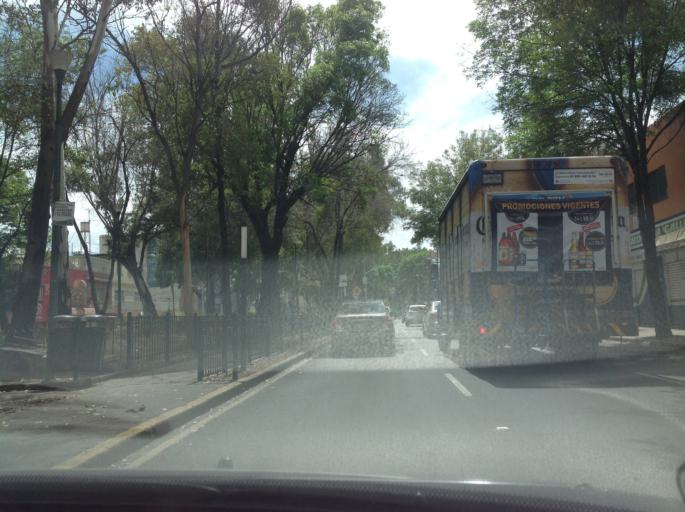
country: MX
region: Mexico City
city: Miguel Hidalgo
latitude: 19.4572
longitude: -99.1932
